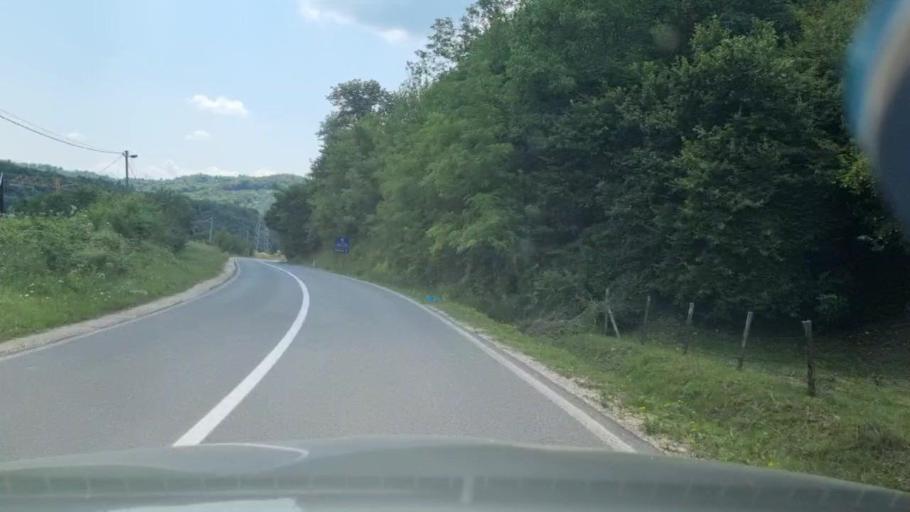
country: BA
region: Federation of Bosnia and Herzegovina
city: Gornja Tuzla
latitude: 44.5326
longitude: 18.7756
